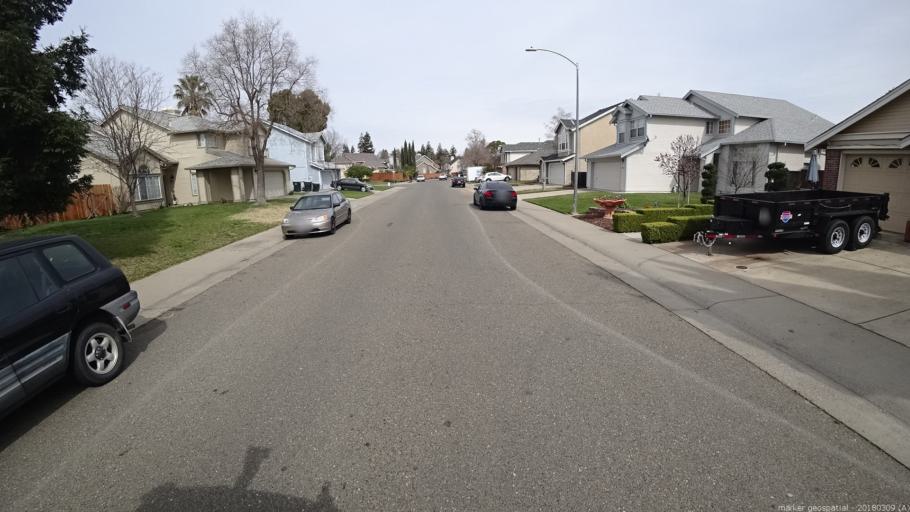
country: US
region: California
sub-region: Sacramento County
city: Vineyard
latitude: 38.4581
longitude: -121.3796
